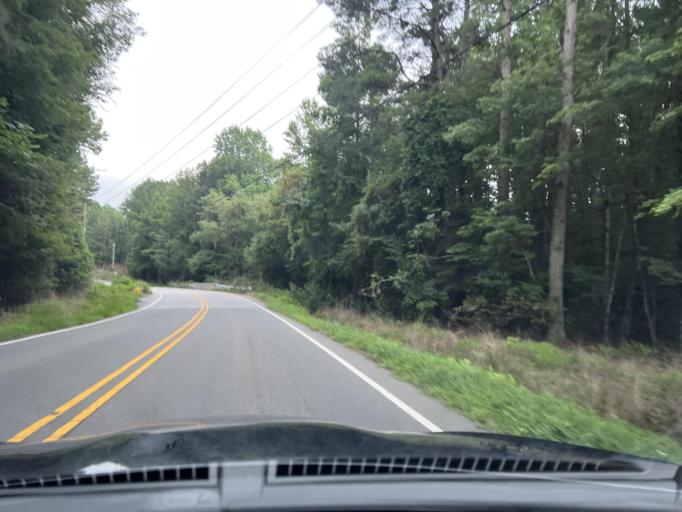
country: US
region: North Carolina
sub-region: Wake County
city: Wake Forest
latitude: 36.0072
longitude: -78.5299
